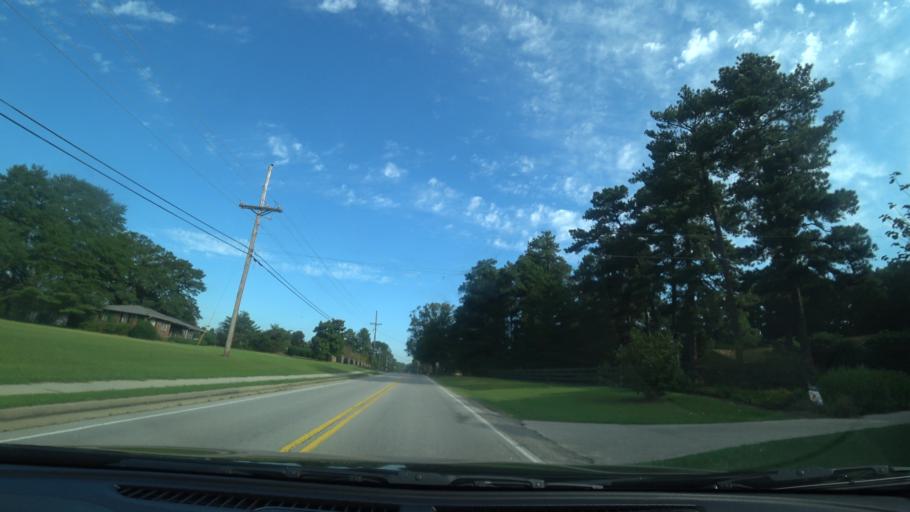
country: US
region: Georgia
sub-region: Gwinnett County
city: Grayson
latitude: 33.8814
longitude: -83.9567
